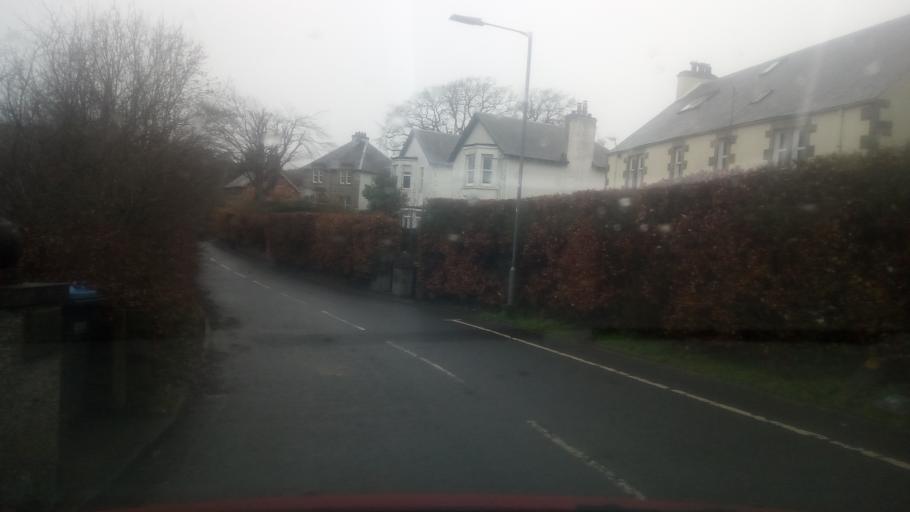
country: GB
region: Scotland
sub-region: The Scottish Borders
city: Earlston
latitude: 55.6350
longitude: -2.6749
